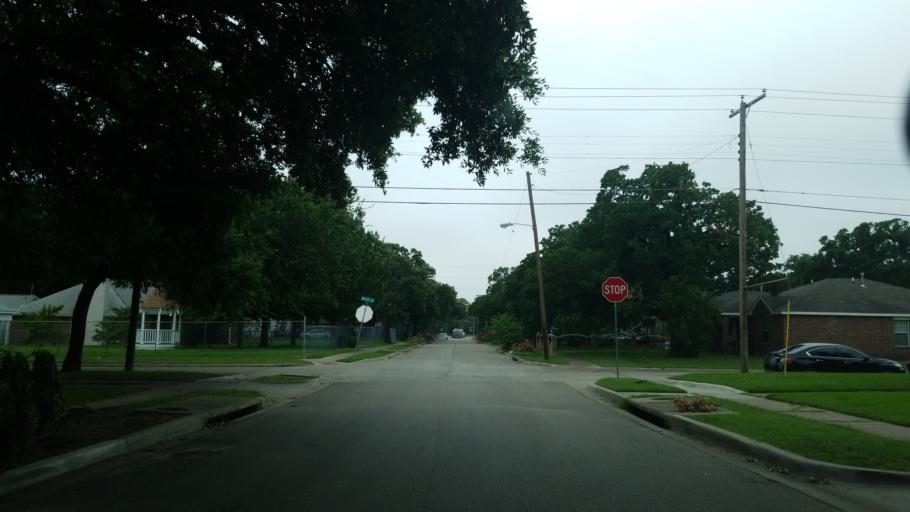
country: US
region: Texas
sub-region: Dallas County
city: University Park
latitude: 32.8355
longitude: -96.8592
